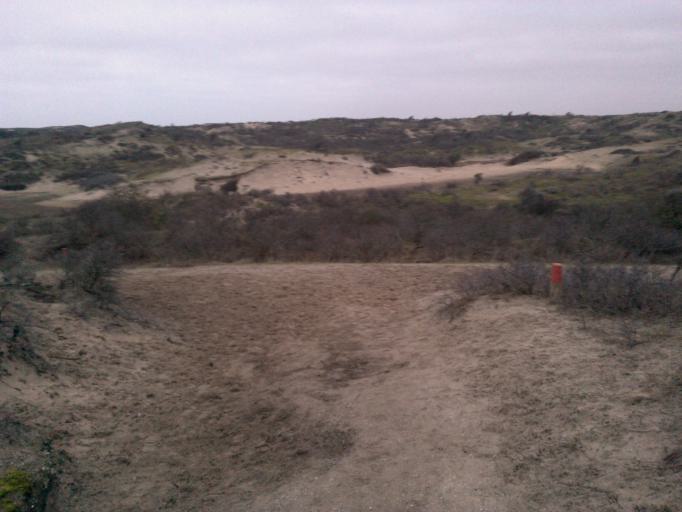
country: NL
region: South Holland
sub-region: Gemeente Noordwijkerhout
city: Noordwijkerhout
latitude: 52.3107
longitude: 4.4890
